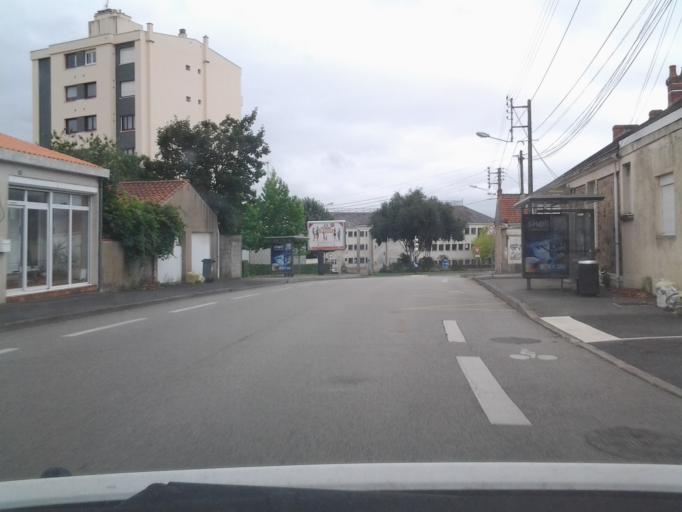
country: FR
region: Pays de la Loire
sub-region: Departement de la Vendee
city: La Roche-sur-Yon
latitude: 46.6763
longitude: -1.4246
